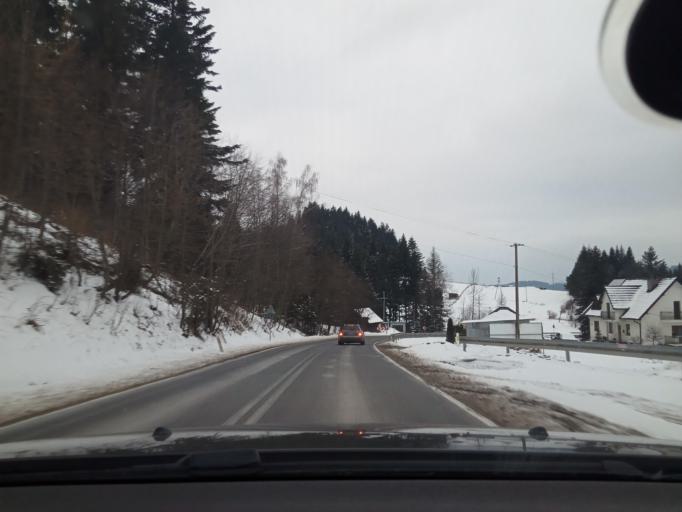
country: PL
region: Lesser Poland Voivodeship
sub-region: Powiat limanowski
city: Lubomierz
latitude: 49.5968
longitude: 20.2166
